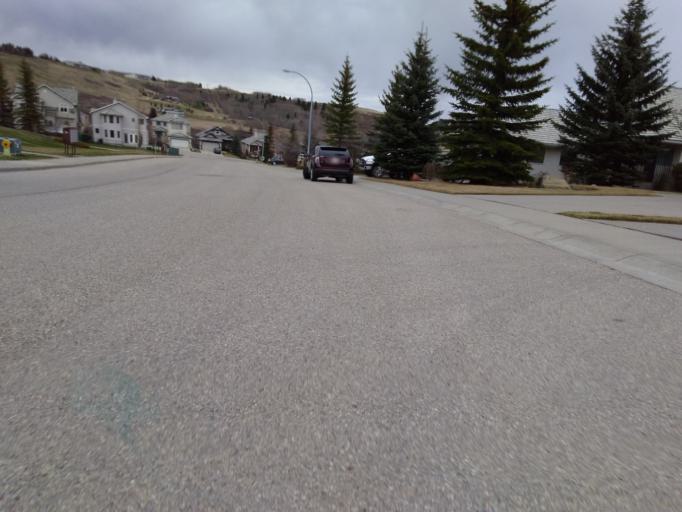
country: CA
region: Alberta
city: Cochrane
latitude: 51.1838
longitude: -114.4252
